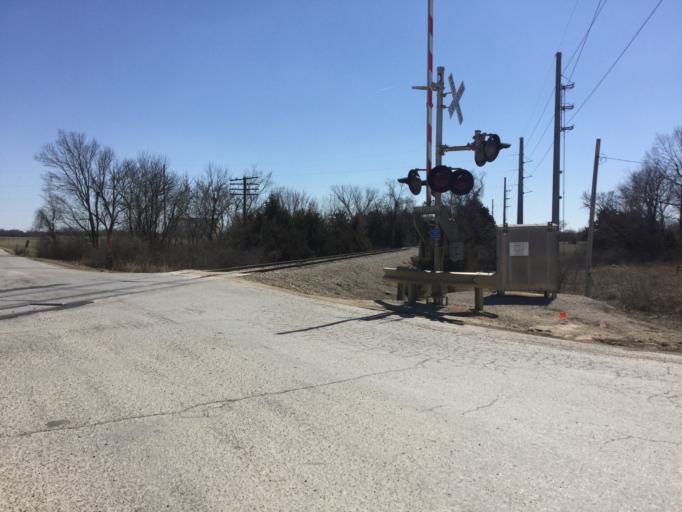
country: US
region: Kansas
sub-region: Allen County
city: Humboldt
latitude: 37.7922
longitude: -95.4290
